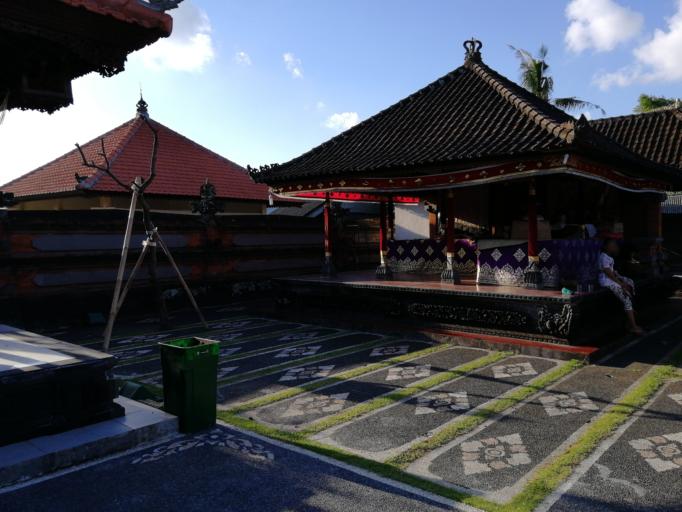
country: ID
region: Bali
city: Banjar Gunungpande
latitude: -8.6101
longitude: 115.1568
